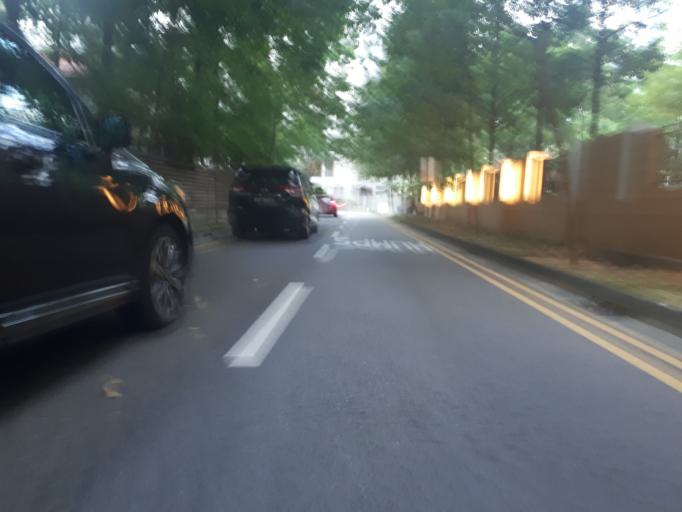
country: SG
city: Singapore
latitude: 1.3152
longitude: 103.8432
